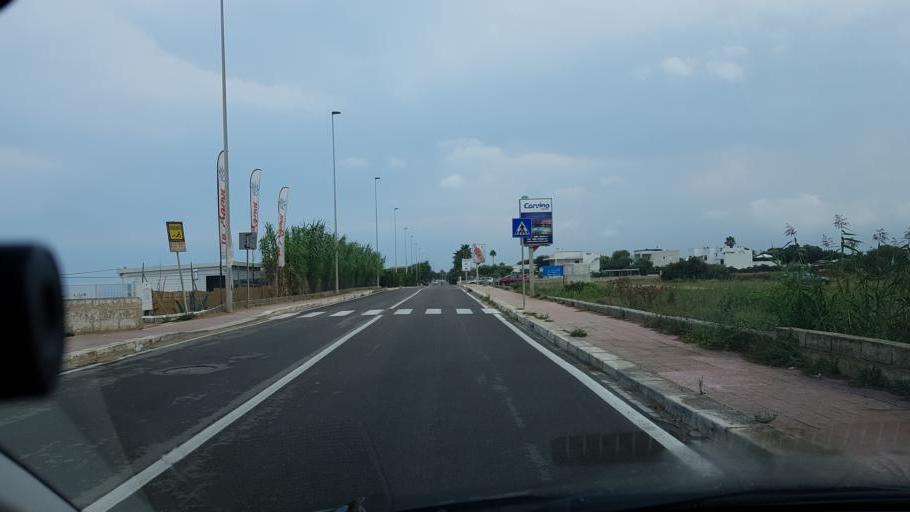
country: IT
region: Apulia
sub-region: Provincia di Brindisi
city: Fasano
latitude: 40.9029
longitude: 17.3545
